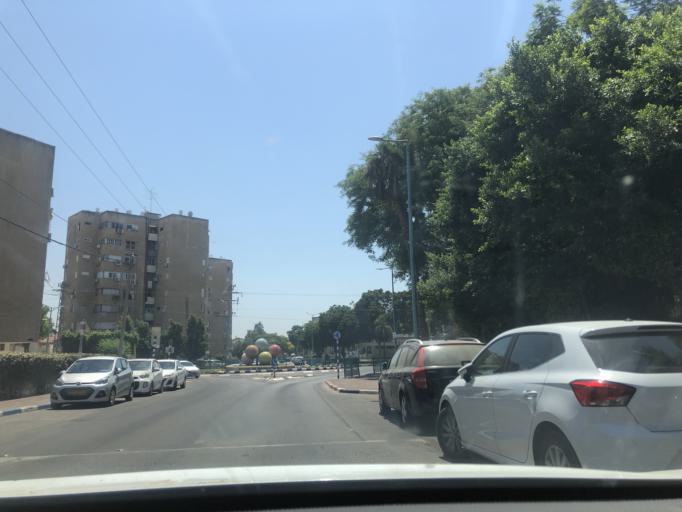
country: IL
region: Central District
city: Lod
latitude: 31.9428
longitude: 34.8914
